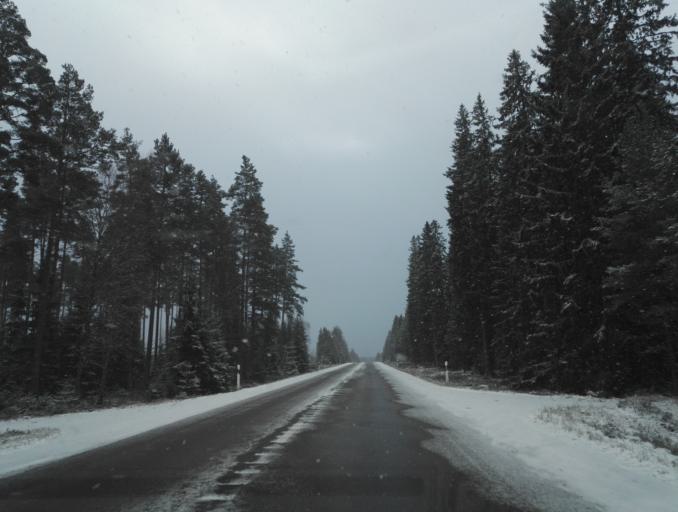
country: SE
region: Kronoberg
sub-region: Uppvidinge Kommun
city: Lenhovda
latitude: 56.9111
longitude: 15.3674
